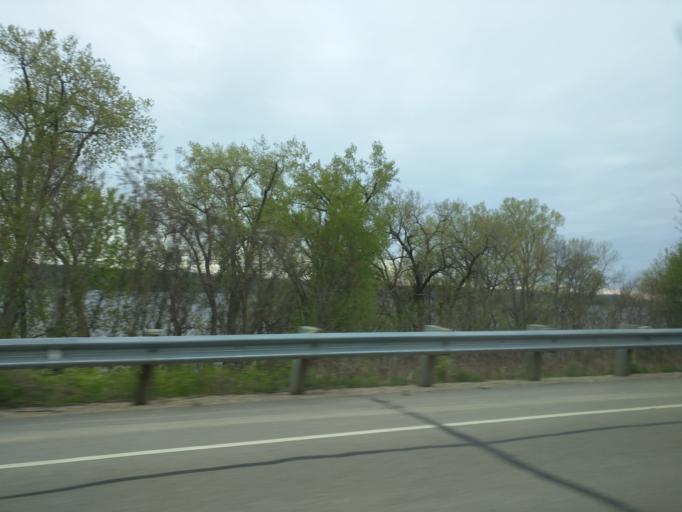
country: US
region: Minnesota
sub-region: Wabasha County
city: Lake City
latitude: 44.5755
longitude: -92.3560
